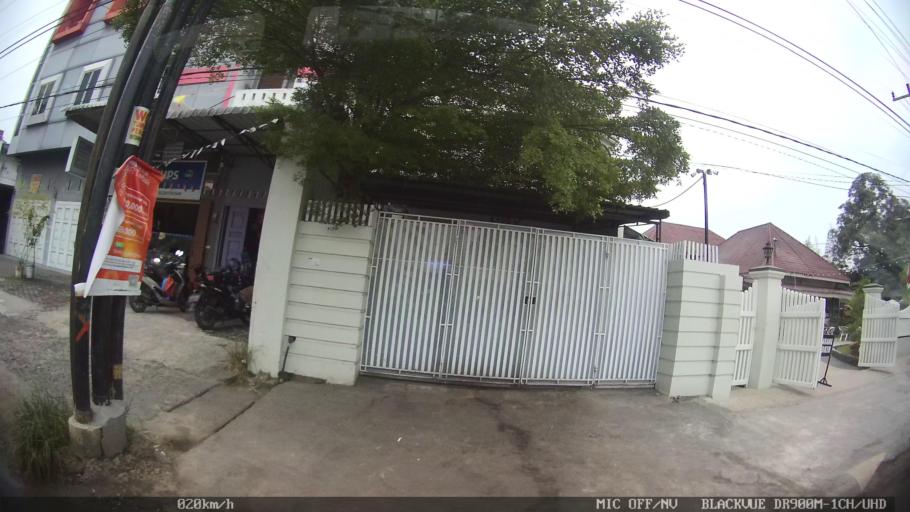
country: ID
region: North Sumatra
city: Medan
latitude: 3.5530
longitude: 98.6950
